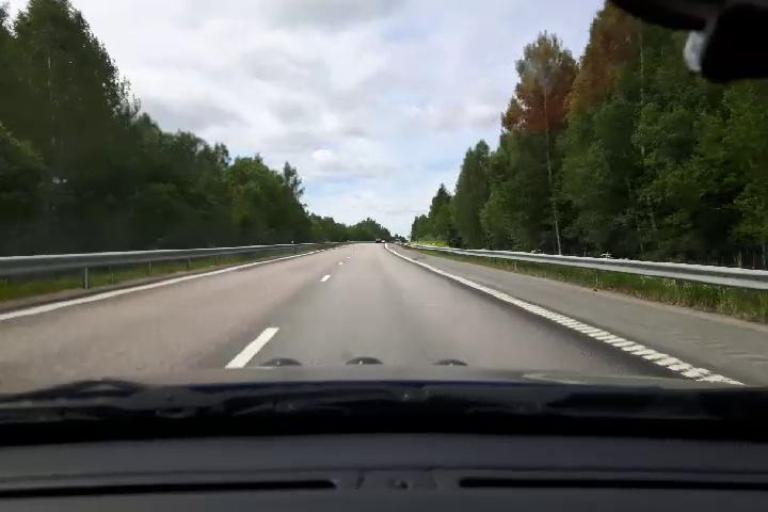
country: SE
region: Uppsala
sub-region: Alvkarleby Kommun
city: AElvkarleby
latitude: 60.4766
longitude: 17.3756
